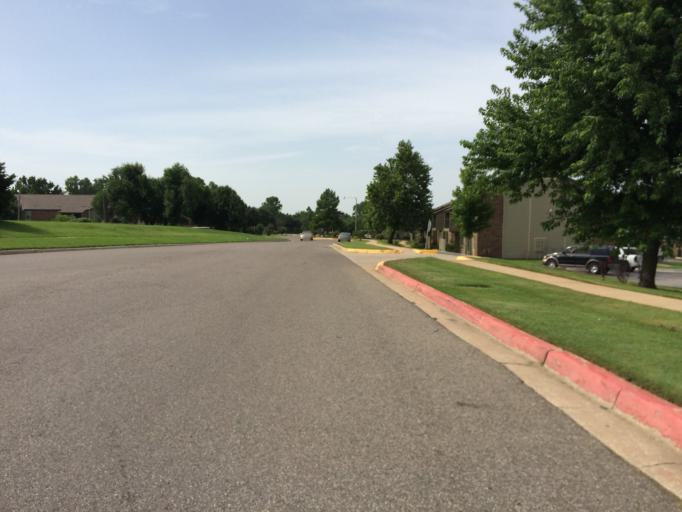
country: US
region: Oklahoma
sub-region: Cleveland County
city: Norman
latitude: 35.2035
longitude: -97.4162
